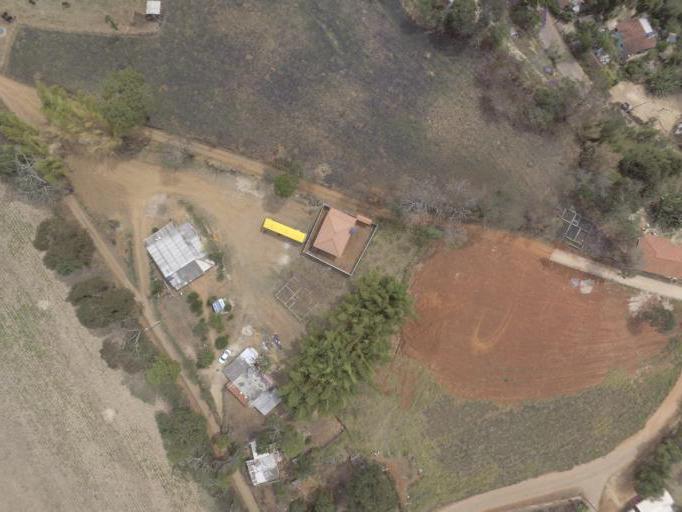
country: BR
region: Minas Gerais
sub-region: Tiradentes
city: Tiradentes
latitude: -21.0570
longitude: -44.0700
